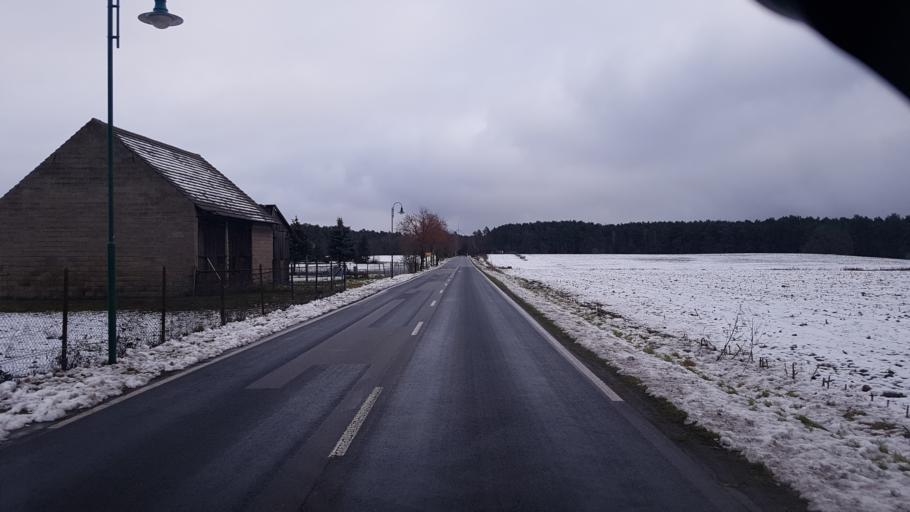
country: DE
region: Brandenburg
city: Schenkendobern
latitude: 51.9778
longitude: 14.5392
